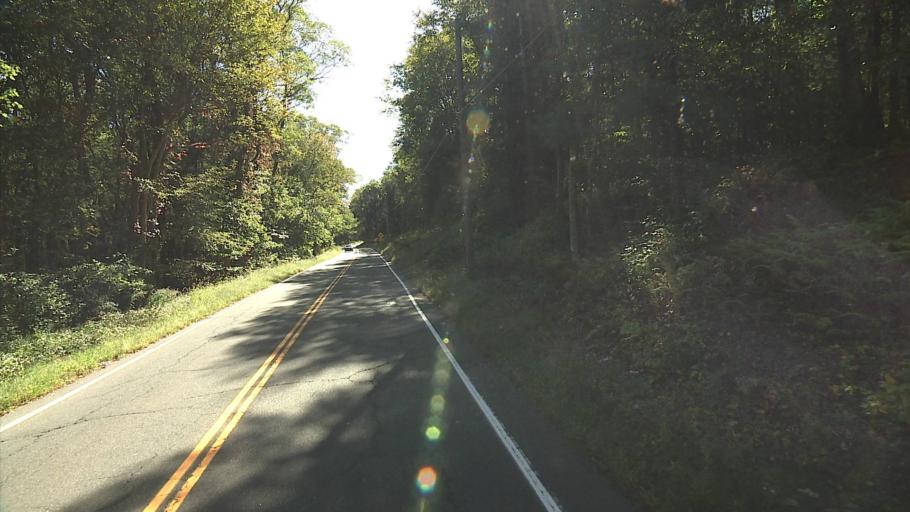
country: US
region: Connecticut
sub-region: Hartford County
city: Bristol
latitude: 41.7357
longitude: -72.9591
